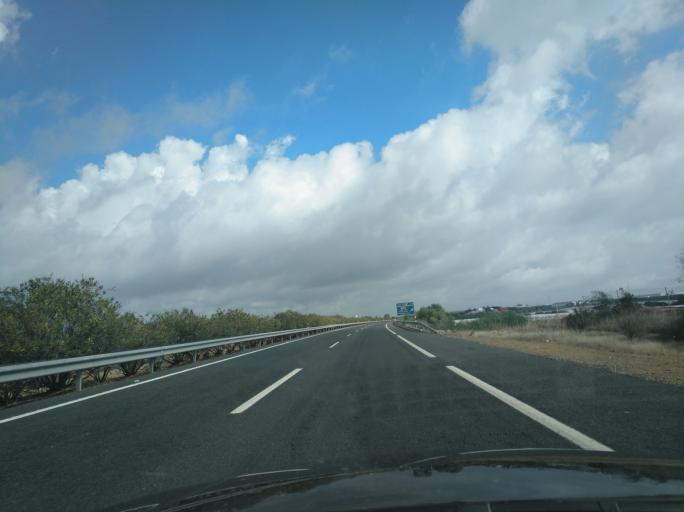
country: ES
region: Andalusia
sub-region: Provincia de Huelva
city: Lepe
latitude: 37.2894
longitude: -7.2333
